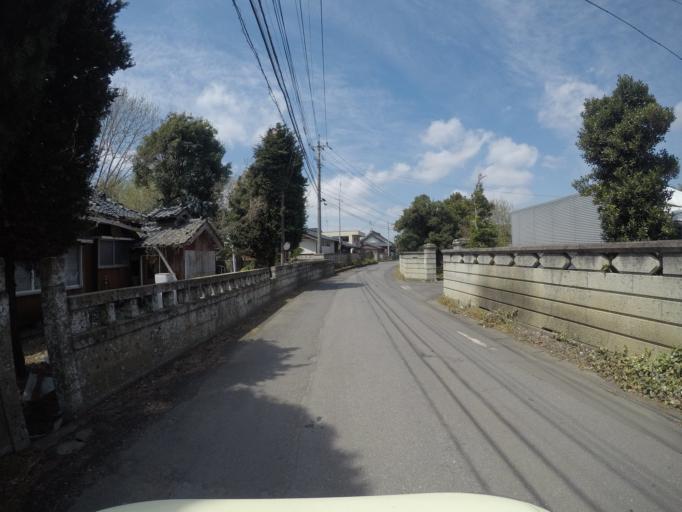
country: JP
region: Ibaraki
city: Shimodate
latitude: 36.2944
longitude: 140.0317
